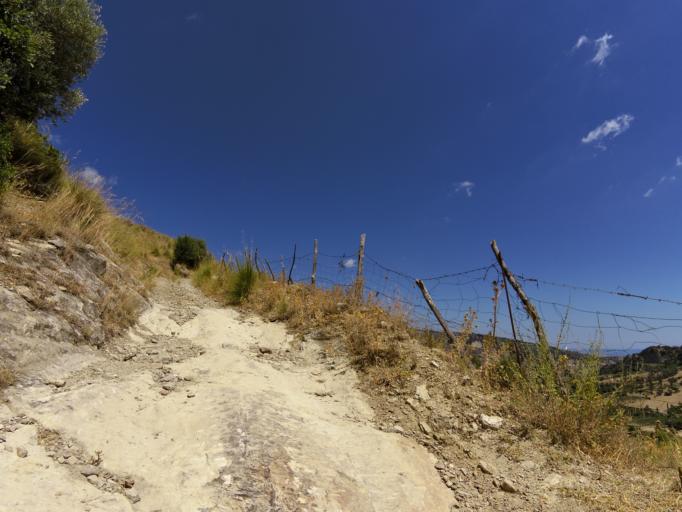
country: IT
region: Calabria
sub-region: Provincia di Reggio Calabria
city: Stilo
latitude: 38.4604
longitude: 16.4626
